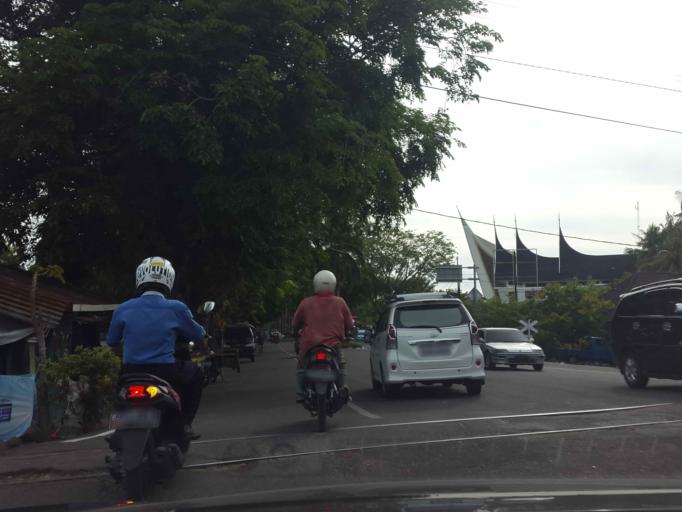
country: ID
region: West Sumatra
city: Padang
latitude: -0.9253
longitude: 100.3658
